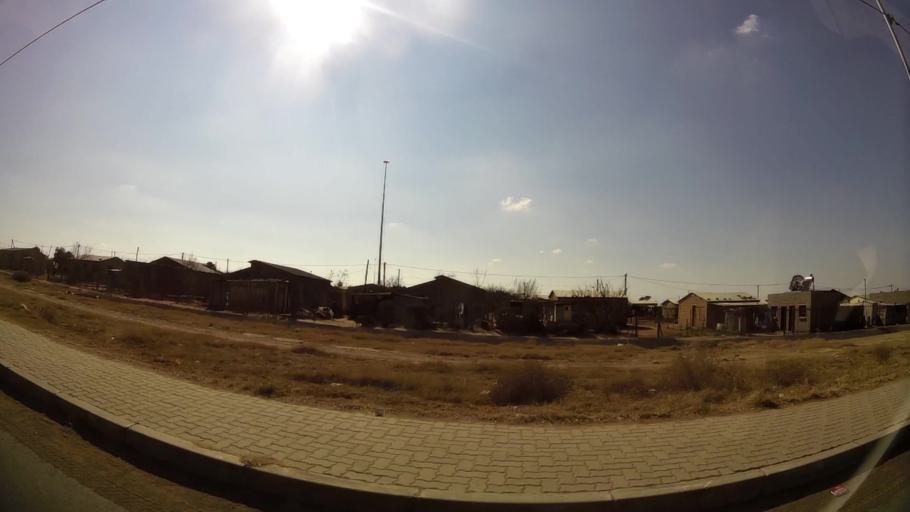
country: ZA
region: Orange Free State
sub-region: Mangaung Metropolitan Municipality
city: Bloemfontein
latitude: -29.1678
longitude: 26.2888
